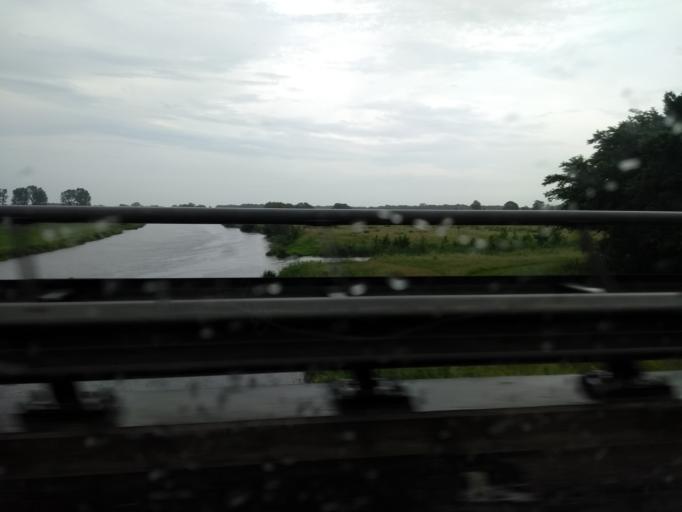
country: NL
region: Overijssel
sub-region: Gemeente Twenterand
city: Vroomshoop
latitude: 52.5153
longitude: 6.5587
